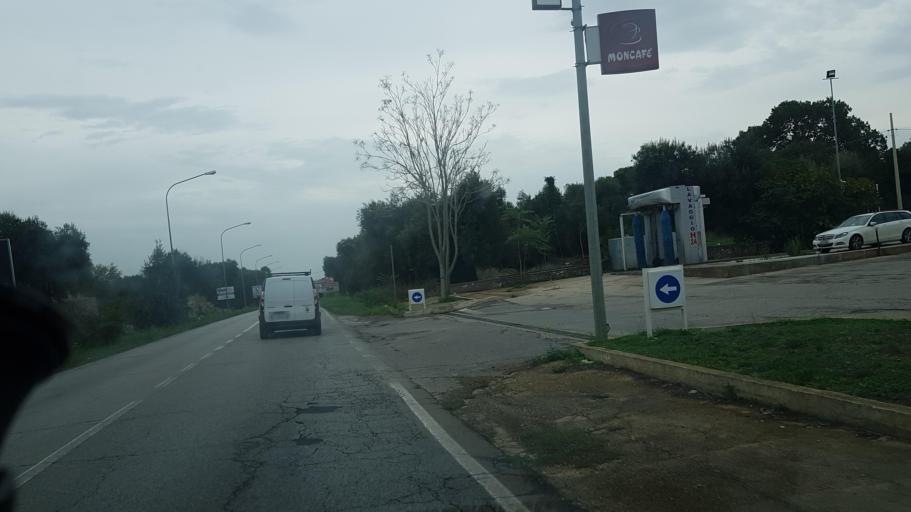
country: IT
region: Apulia
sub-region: Provincia di Brindisi
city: Ostuni
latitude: 40.7237
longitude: 17.5973
